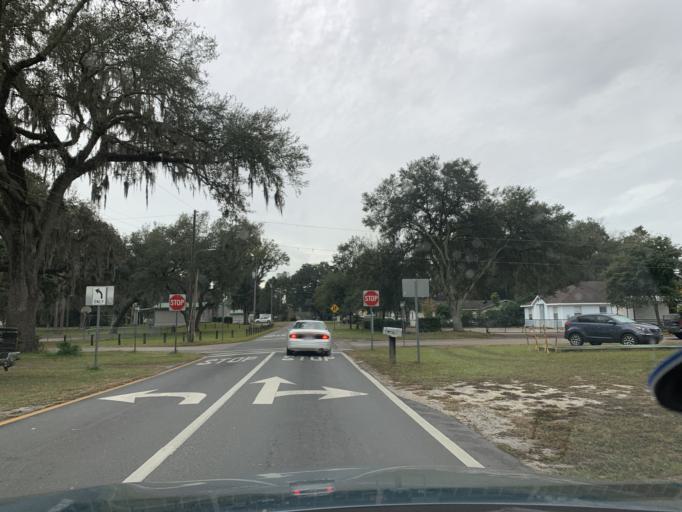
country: US
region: Florida
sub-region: Pasco County
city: Zephyrhills
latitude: 28.2292
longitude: -82.1811
